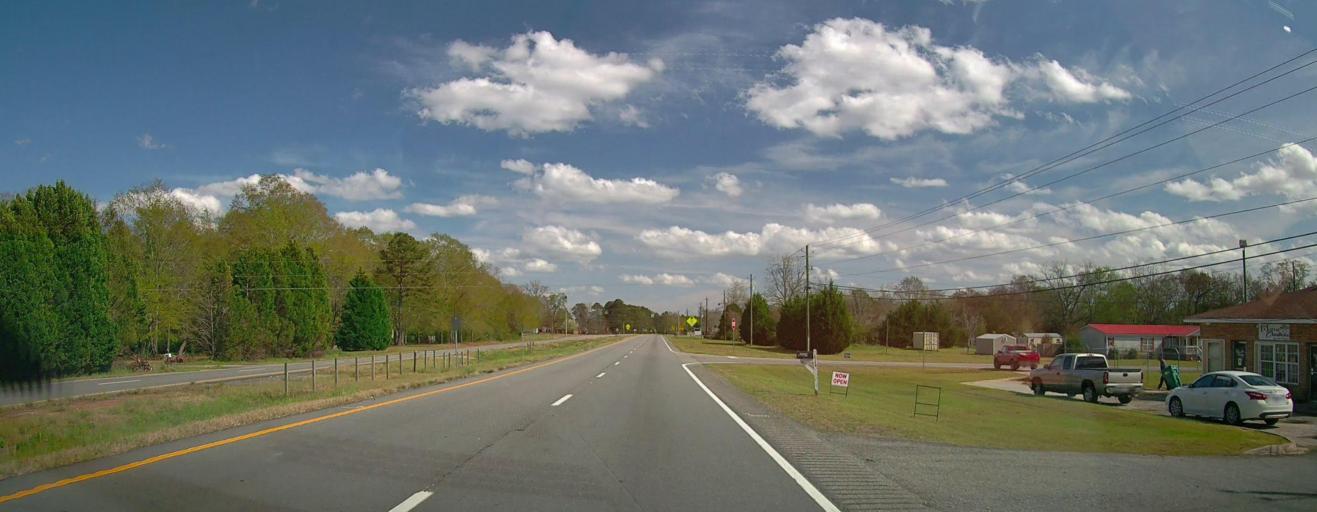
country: US
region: Georgia
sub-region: Baldwin County
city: Hardwick
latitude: 33.0220
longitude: -83.2320
